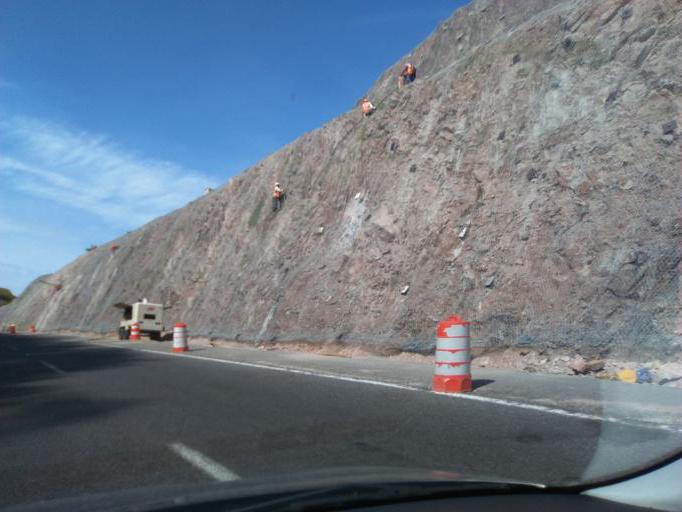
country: MX
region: Guerrero
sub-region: Huitzuco de los Figueroa
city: Ciudad de Huitzuco
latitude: 18.1877
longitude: -99.2036
